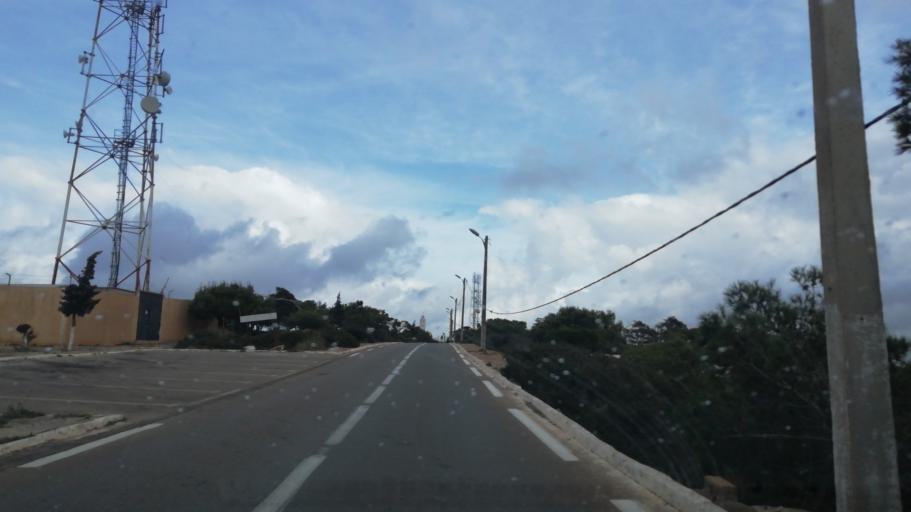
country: DZ
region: Oran
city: Oran
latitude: 35.7036
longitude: -0.6759
